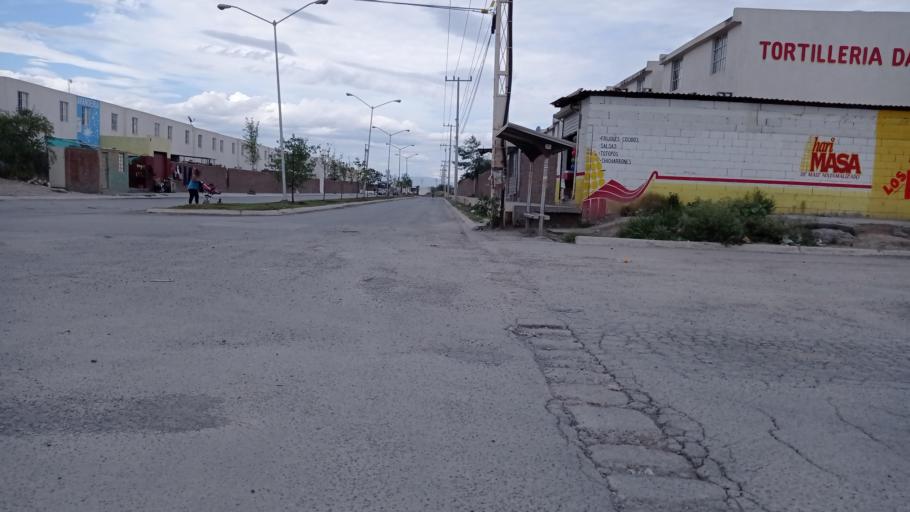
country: MX
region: Nuevo Leon
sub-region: Salinas Victoria
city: Simeprodeso (Colectivo Nuevo)
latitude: 25.8746
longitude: -100.3139
